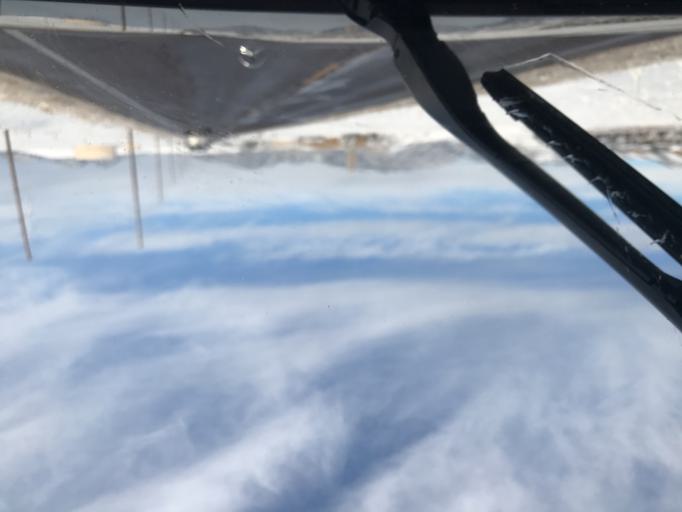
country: US
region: Colorado
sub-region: Boulder County
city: Superior
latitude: 39.8551
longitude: -105.1863
